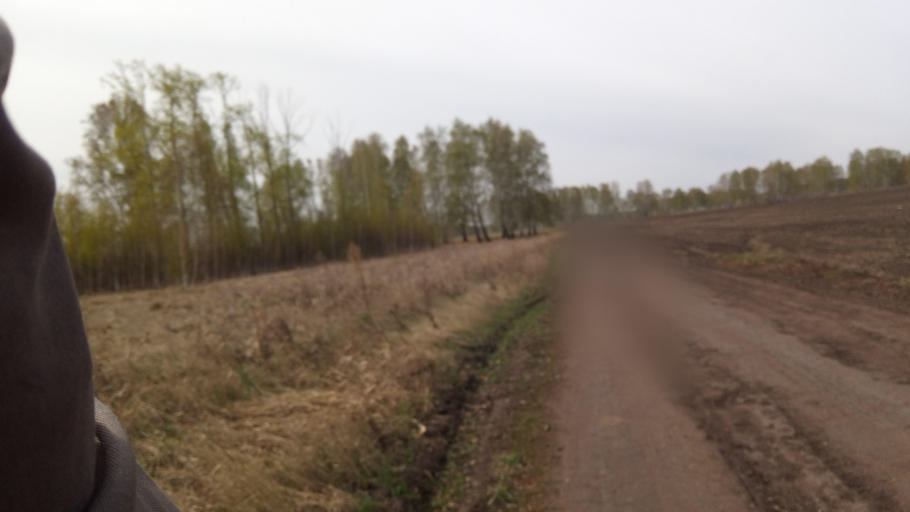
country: RU
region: Chelyabinsk
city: Timiryazevskiy
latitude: 55.0255
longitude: 60.8526
